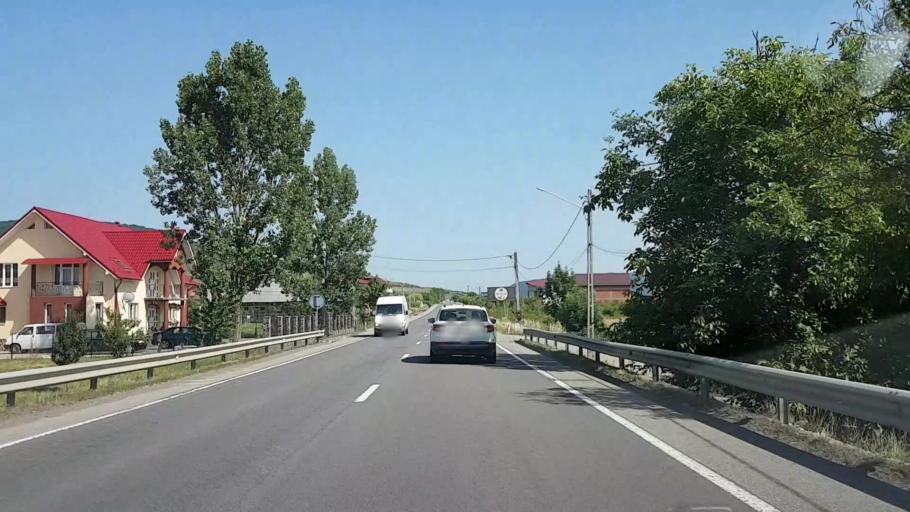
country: RO
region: Bistrita-Nasaud
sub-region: Comuna Sieu-Magherus
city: Sieu-Magherus
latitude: 47.0869
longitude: 24.3814
